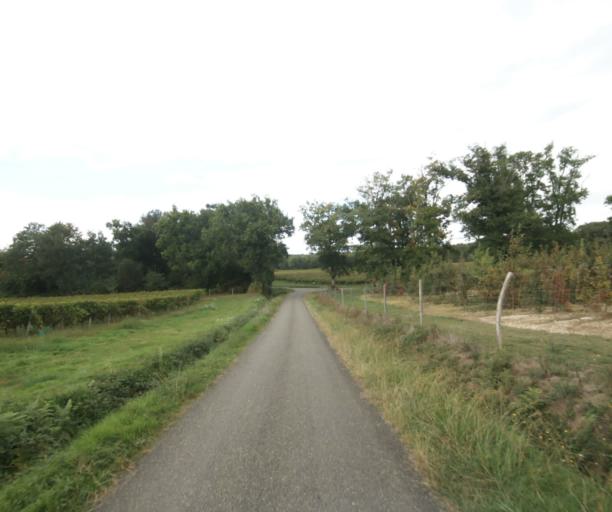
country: FR
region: Midi-Pyrenees
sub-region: Departement du Gers
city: Eauze
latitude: 43.9044
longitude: 0.1200
